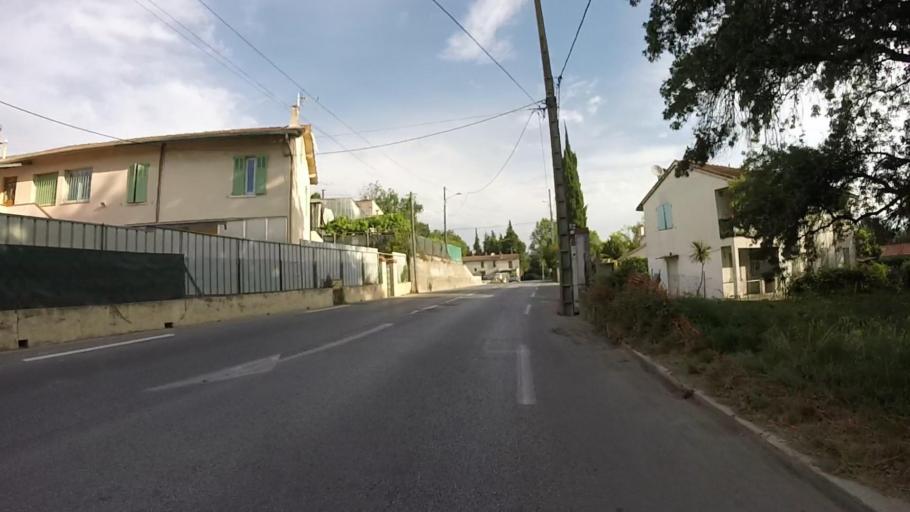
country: FR
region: Provence-Alpes-Cote d'Azur
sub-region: Departement des Alpes-Maritimes
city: Biot
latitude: 43.6095
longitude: 7.1102
